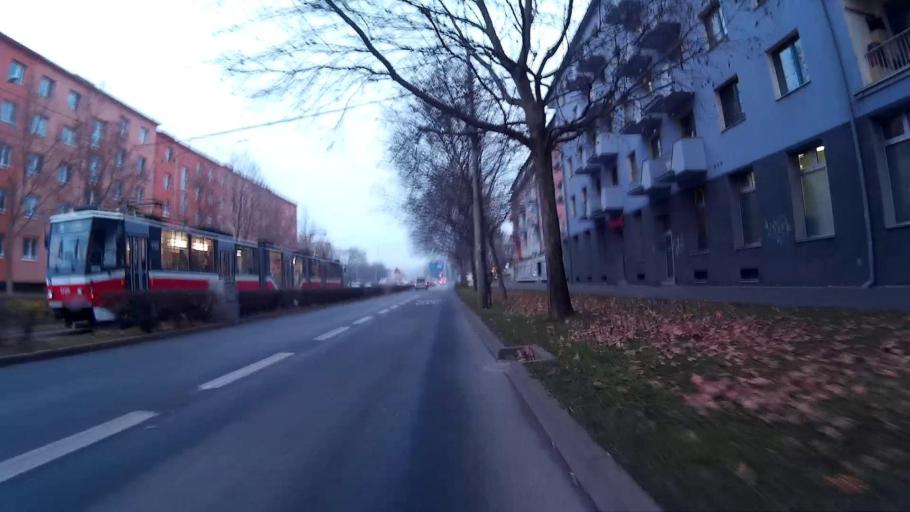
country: CZ
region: South Moravian
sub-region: Mesto Brno
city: Brno
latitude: 49.1867
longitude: 16.6047
